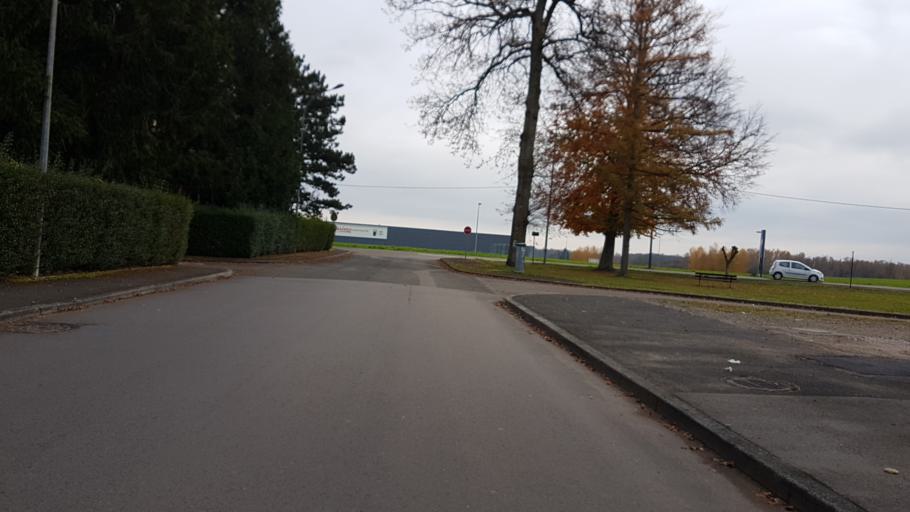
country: FR
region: Franche-Comte
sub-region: Departement de la Haute-Saone
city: Luxeuil-les-Bains
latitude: 47.8112
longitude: 6.3589
